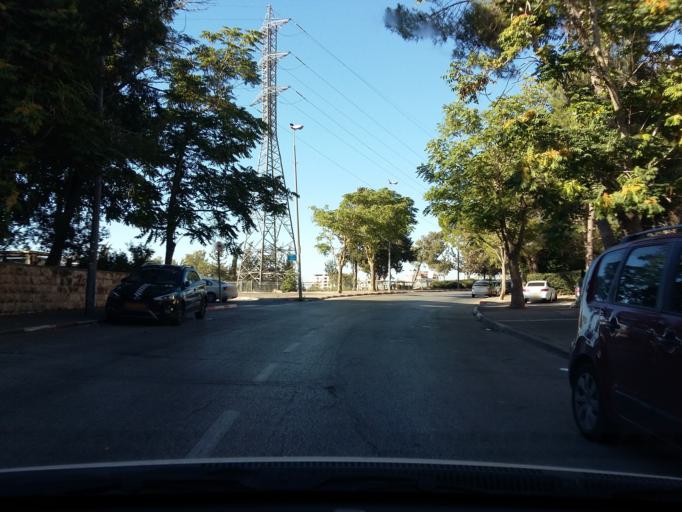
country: PS
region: West Bank
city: `Anata
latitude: 31.8069
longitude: 35.2376
